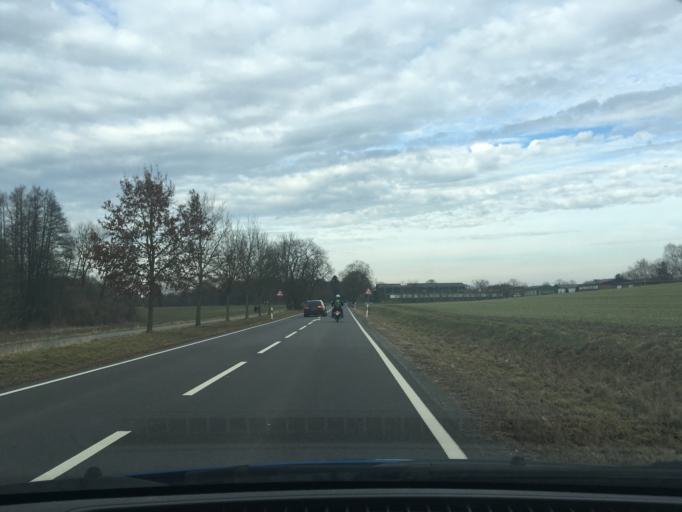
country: DE
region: Mecklenburg-Vorpommern
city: Boizenburg
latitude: 53.4207
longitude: 10.7456
